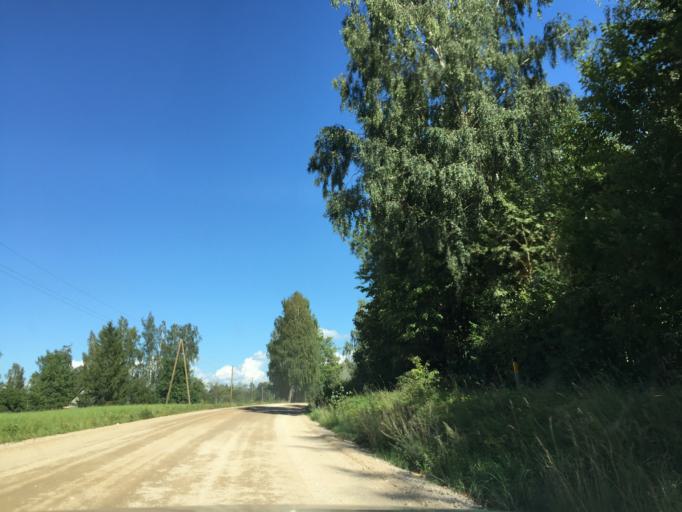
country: LV
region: Limbazu Rajons
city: Limbazi
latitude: 57.5476
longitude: 24.7610
